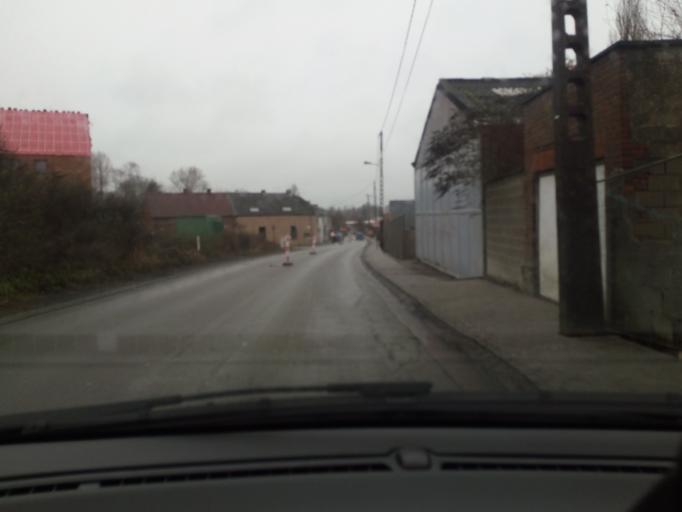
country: BE
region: Wallonia
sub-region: Province du Hainaut
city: Colfontaine
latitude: 50.4242
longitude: 3.8645
